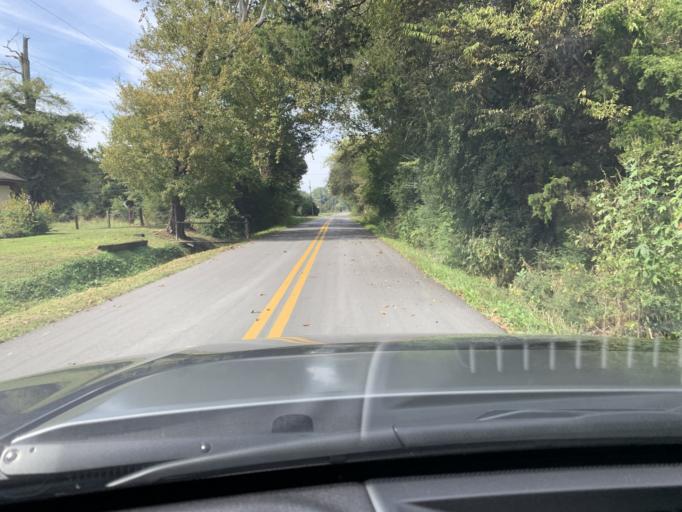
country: US
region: Georgia
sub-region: Floyd County
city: Cave Spring
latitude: 33.9491
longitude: -85.3855
